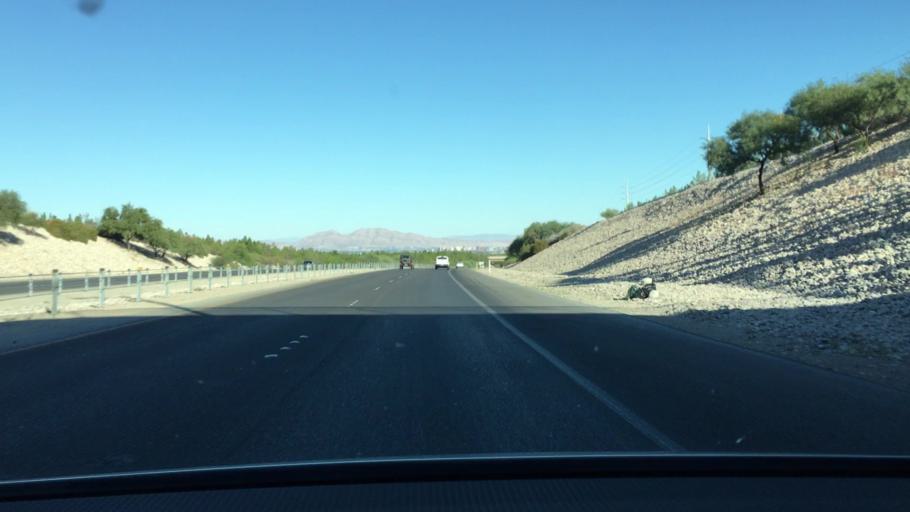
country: US
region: Nevada
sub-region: Clark County
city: Summerlin South
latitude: 36.1935
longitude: -115.3235
